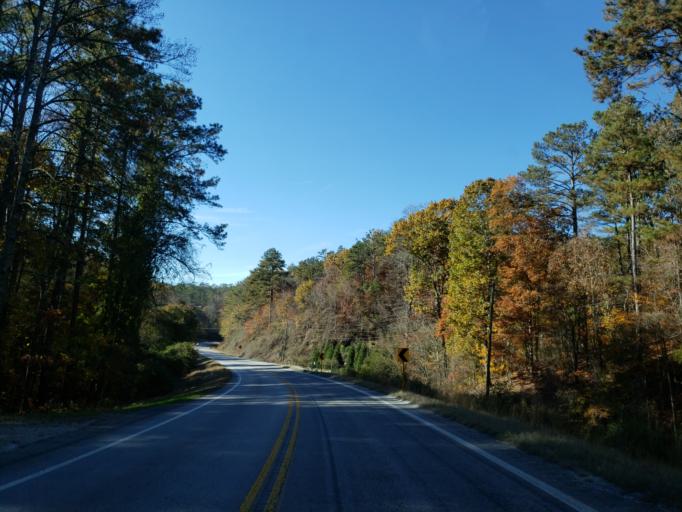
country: US
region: Alabama
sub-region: Calhoun County
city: Choccolocco
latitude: 33.5901
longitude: -85.6856
